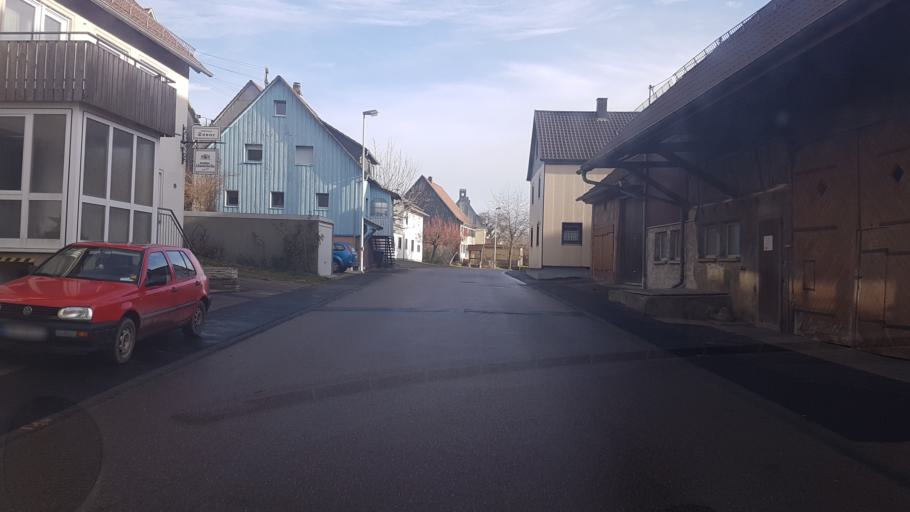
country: DE
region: Baden-Wuerttemberg
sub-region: Regierungsbezirk Stuttgart
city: Wolpertshausen
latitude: 49.2070
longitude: 9.8635
